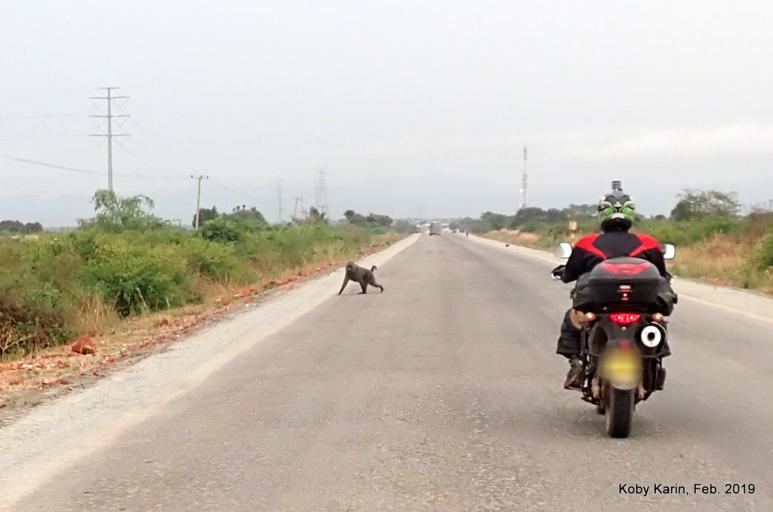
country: UG
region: Western Region
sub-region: Rubirizi District
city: Rubirizi
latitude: -0.1098
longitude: 30.0432
